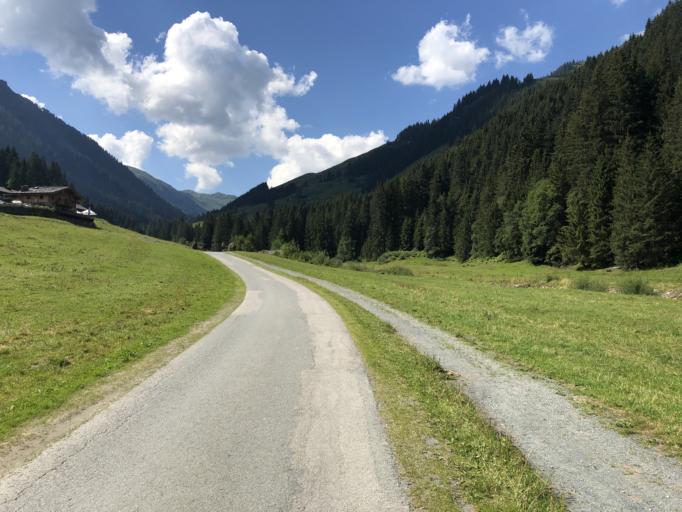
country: AT
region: Tyrol
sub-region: Politischer Bezirk Kitzbuhel
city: Kirchberg in Tirol
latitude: 47.3578
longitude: 12.2893
